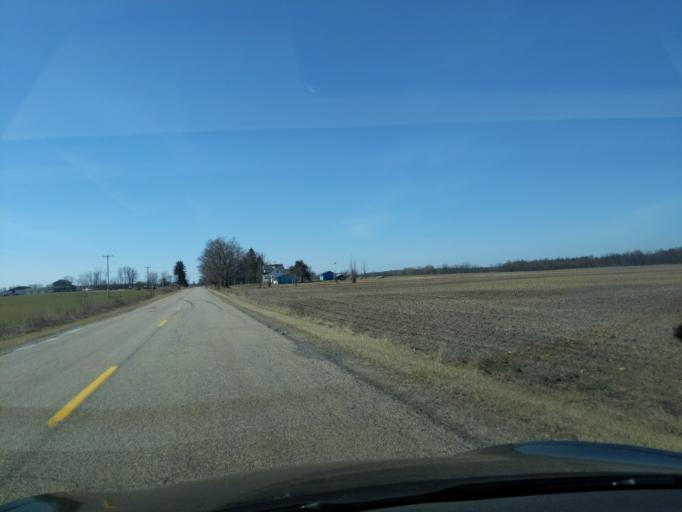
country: US
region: Michigan
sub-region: Ionia County
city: Portland
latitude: 42.7267
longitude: -84.9365
